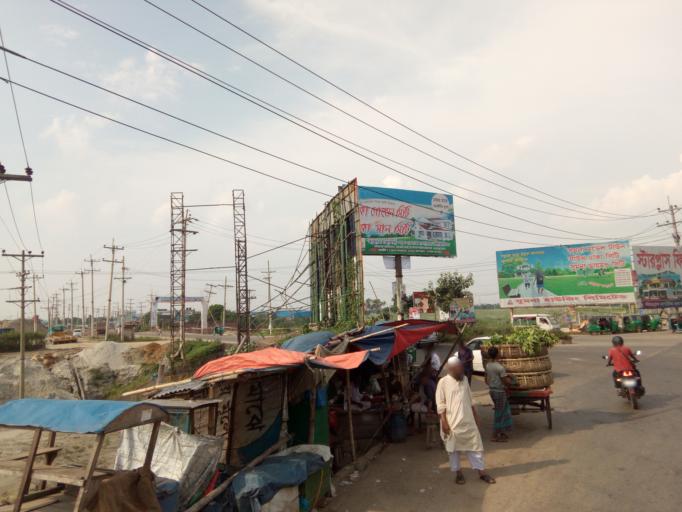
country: BD
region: Dhaka
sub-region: Dhaka
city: Dhaka
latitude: 23.6748
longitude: 90.4050
